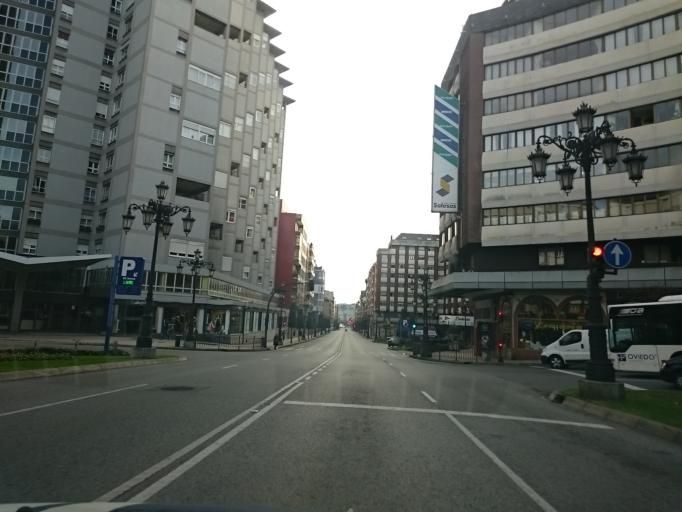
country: ES
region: Asturias
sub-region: Province of Asturias
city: Oviedo
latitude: 43.3634
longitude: -5.8389
